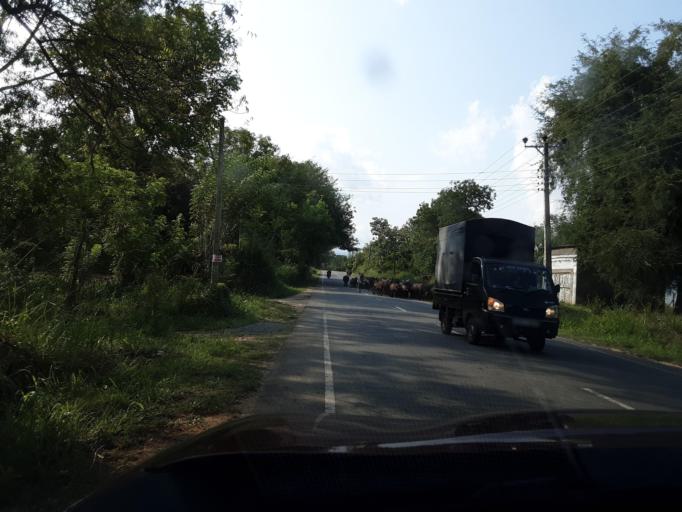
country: LK
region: Uva
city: Haputale
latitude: 6.6070
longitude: 81.1355
